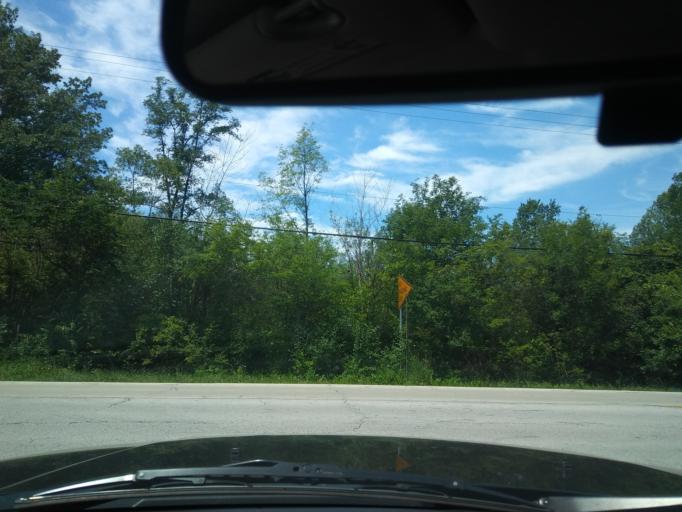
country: US
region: Illinois
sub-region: Cook County
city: Oak Forest
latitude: 41.5995
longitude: -87.7558
